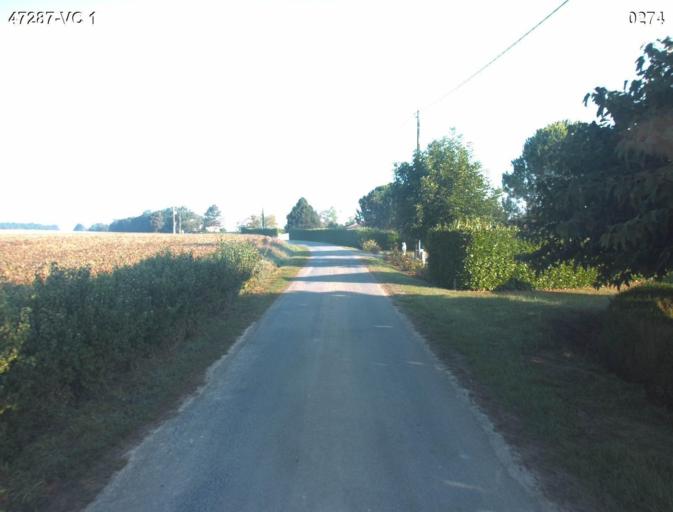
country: FR
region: Aquitaine
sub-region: Departement du Lot-et-Garonne
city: Laplume
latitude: 44.1259
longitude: 0.4572
